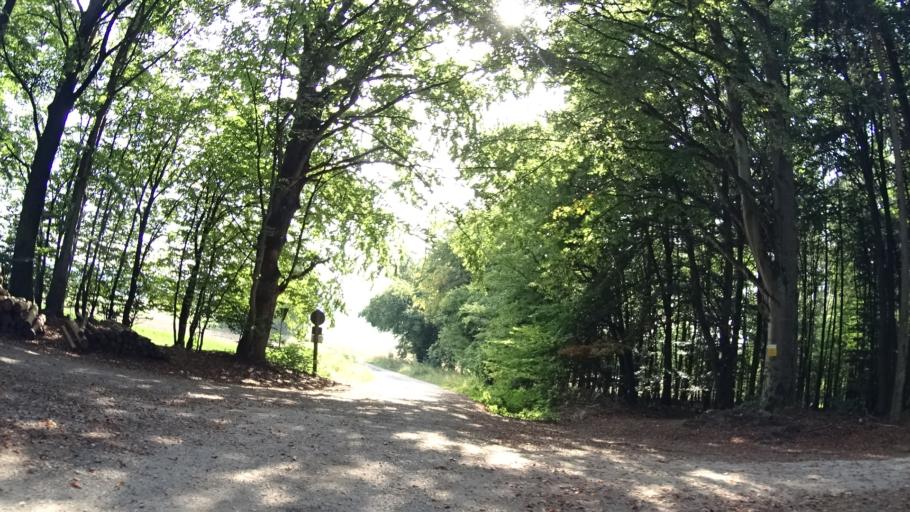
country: DE
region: Bavaria
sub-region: Lower Bavaria
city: Riedenburg
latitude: 48.9712
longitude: 11.6723
